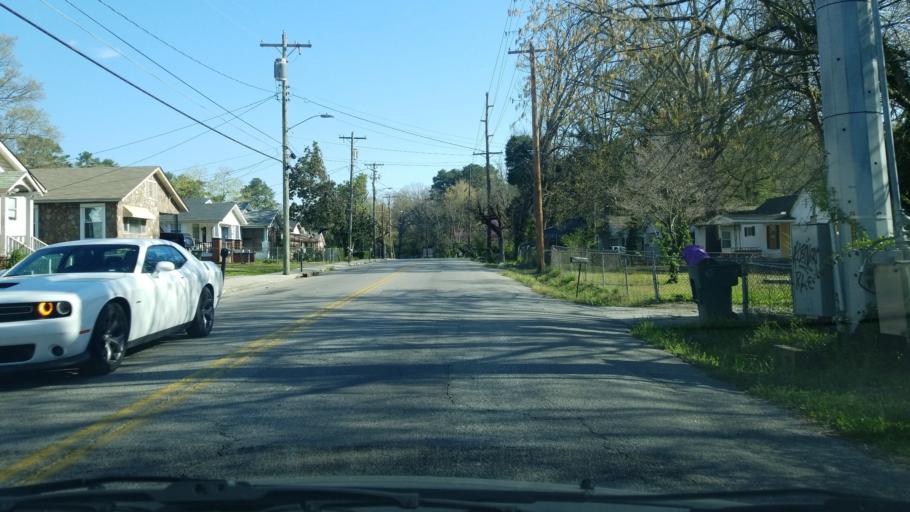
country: US
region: Tennessee
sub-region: Hamilton County
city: East Chattanooga
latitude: 35.0426
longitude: -85.2386
